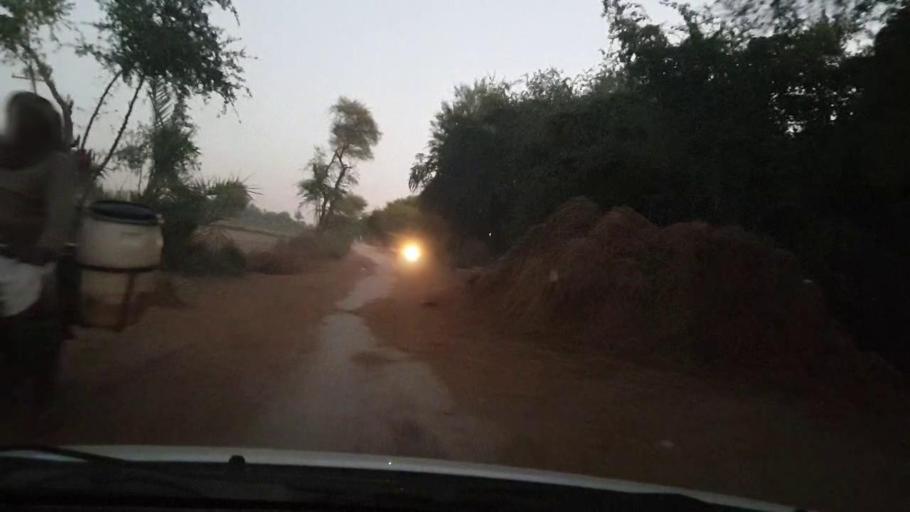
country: PK
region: Sindh
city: Khairpur Nathan Shah
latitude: 27.1353
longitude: 67.7204
